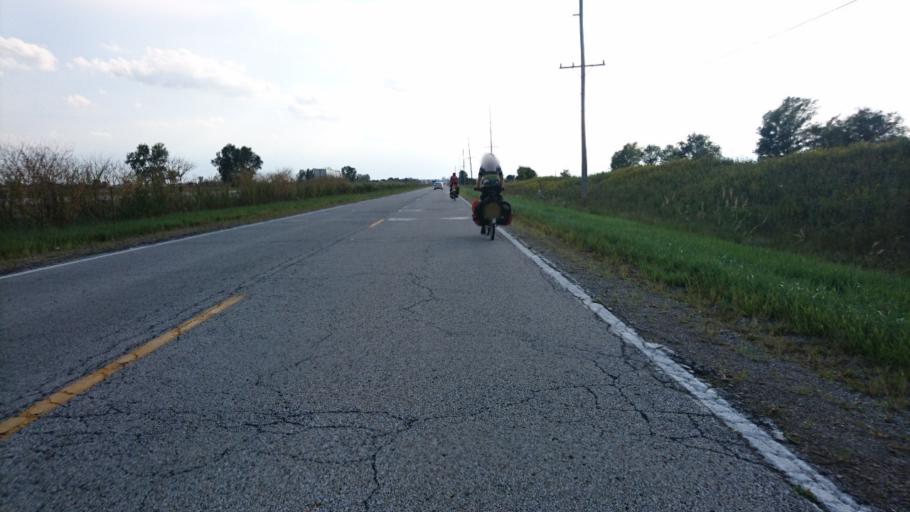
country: US
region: Illinois
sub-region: Logan County
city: Atlanta
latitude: 40.2943
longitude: -89.1930
